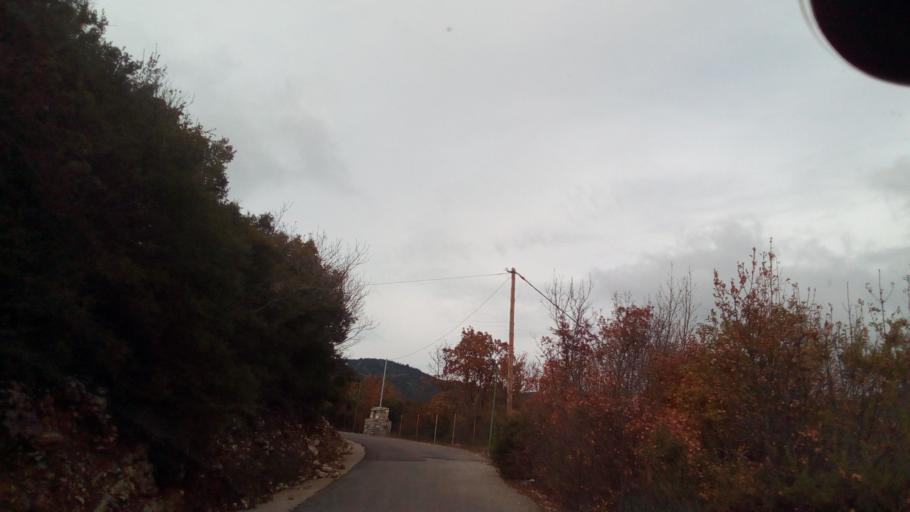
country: GR
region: West Greece
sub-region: Nomos Aitolias kai Akarnanias
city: Thermo
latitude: 38.5954
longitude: 21.7920
